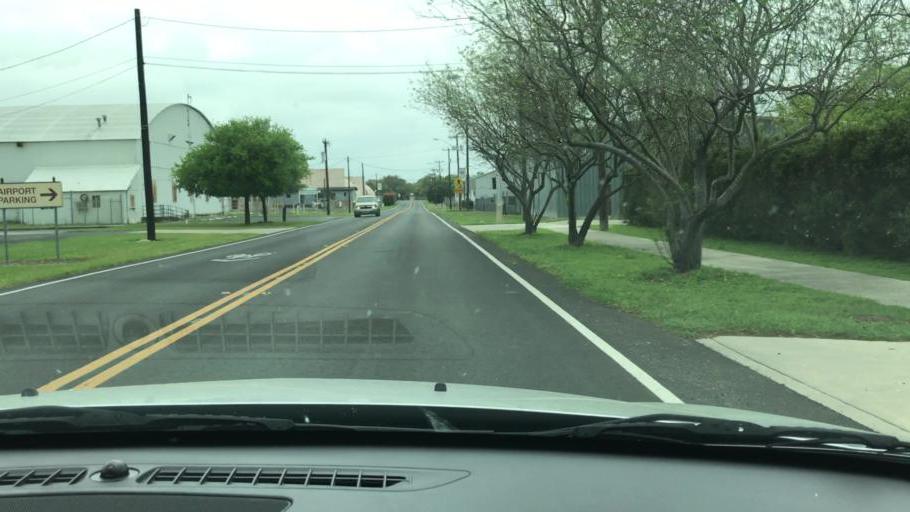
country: US
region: Texas
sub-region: Bexar County
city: San Antonio
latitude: 29.3397
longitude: -98.4682
